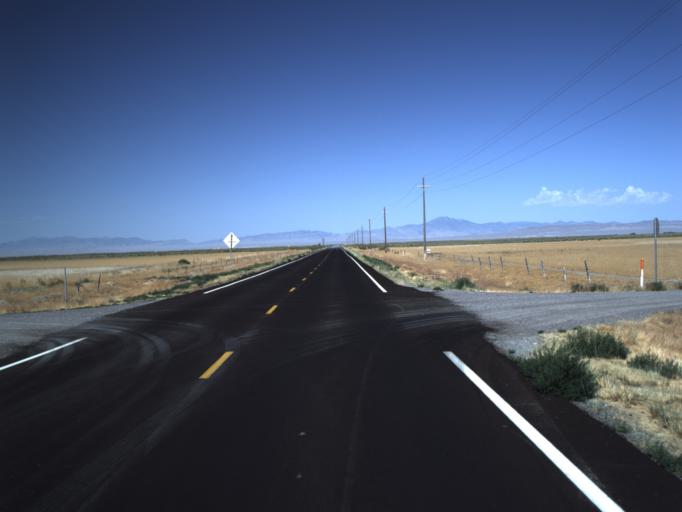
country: US
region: Utah
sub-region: Millard County
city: Delta
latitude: 39.3309
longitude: -112.6941
